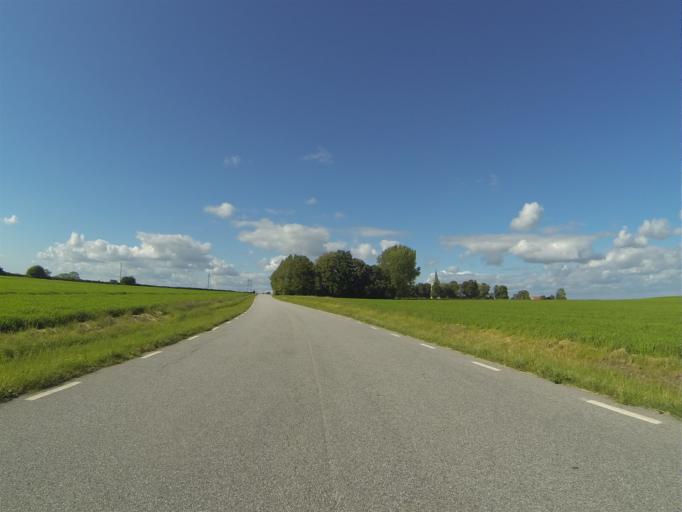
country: SE
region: Skane
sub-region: Staffanstorps Kommun
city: Hjaerup
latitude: 55.6629
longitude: 13.1684
